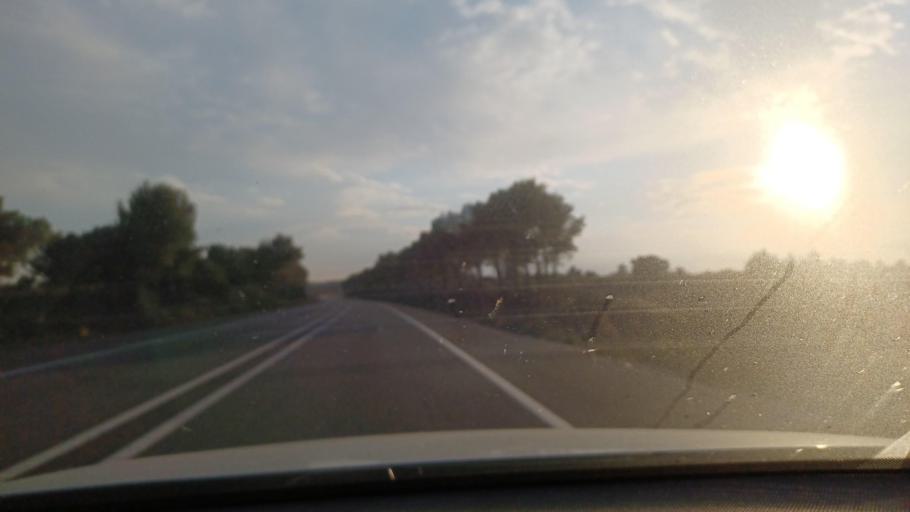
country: ES
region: Catalonia
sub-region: Provincia de Tarragona
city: l'Ametlla de Mar
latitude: 40.9265
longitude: 0.8285
